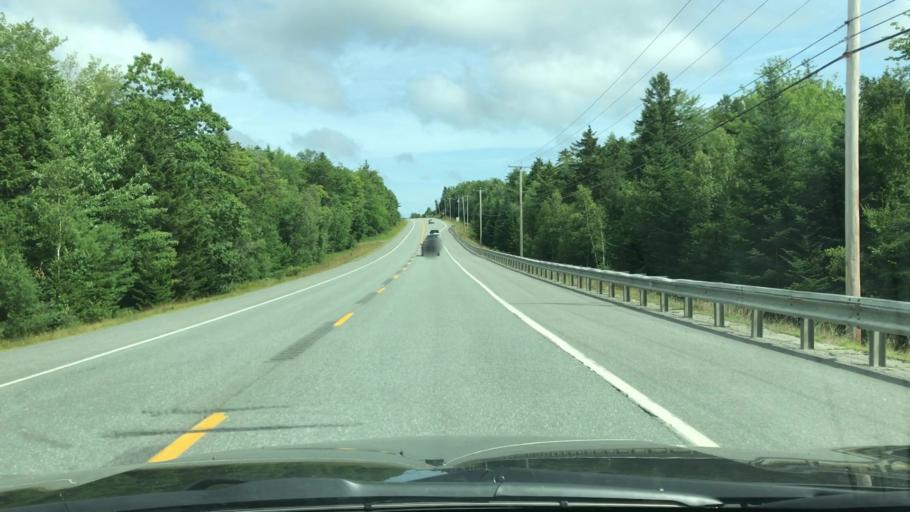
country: US
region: Maine
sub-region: Hancock County
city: Surry
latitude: 44.5493
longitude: -68.5277
